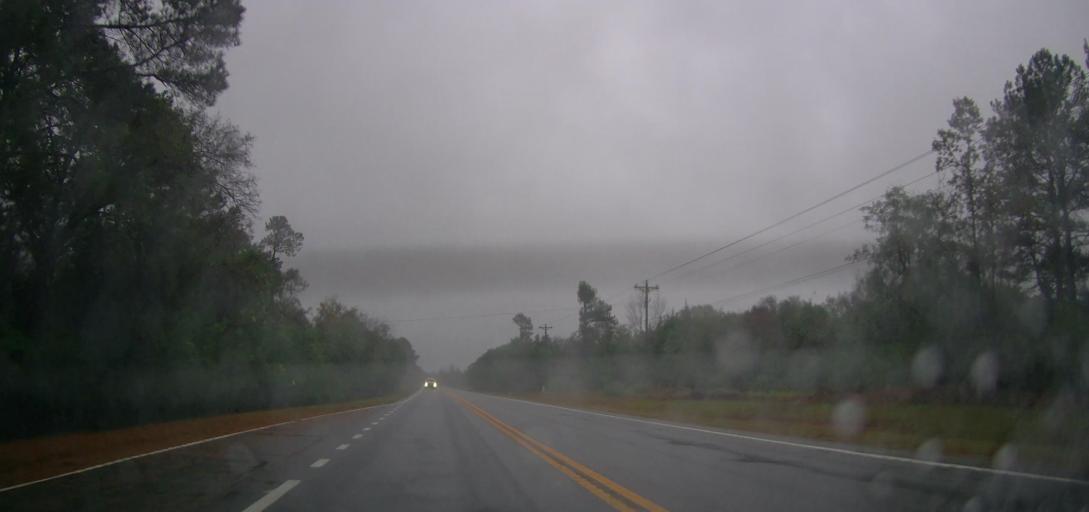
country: US
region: Georgia
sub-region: Jones County
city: Gray
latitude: 33.0371
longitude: -83.5156
